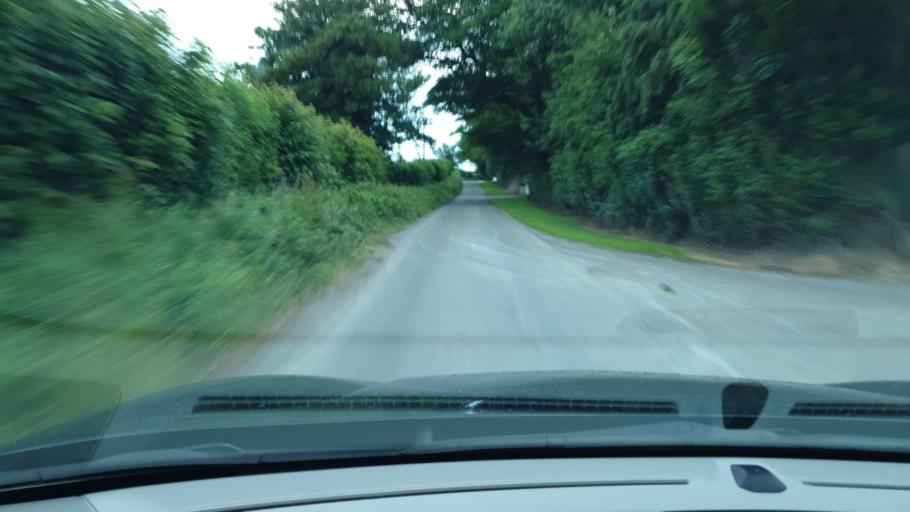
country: IE
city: Kentstown
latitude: 53.5915
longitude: -6.5682
